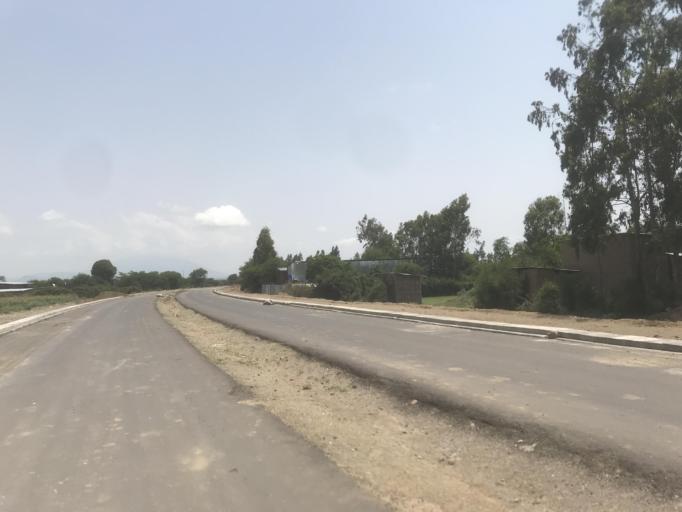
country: ET
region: Oromiya
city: Mojo
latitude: 8.2936
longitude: 38.9404
